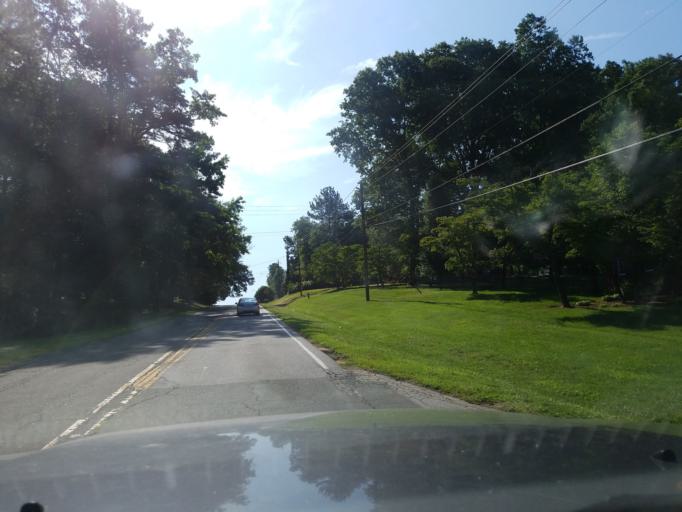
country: US
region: North Carolina
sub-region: Granville County
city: Oxford
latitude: 36.3139
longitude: -78.5613
